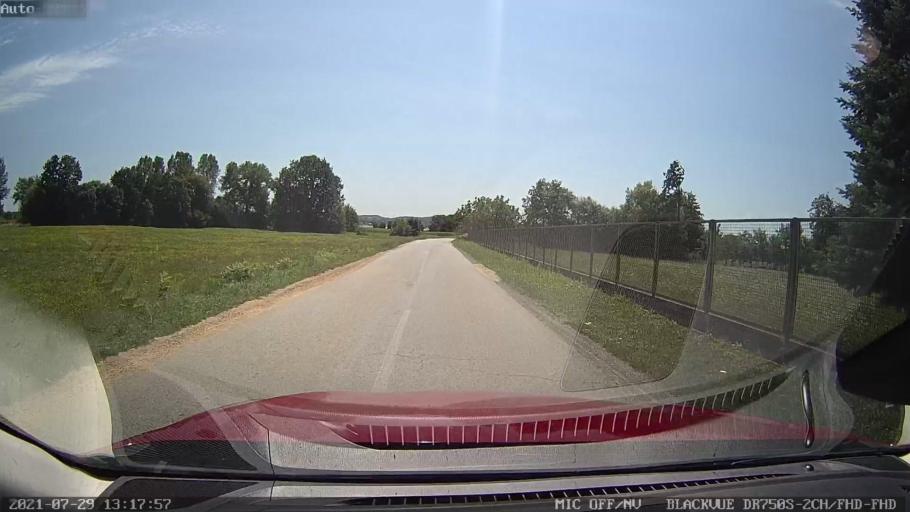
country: HR
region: Varazdinska
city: Varazdin
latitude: 46.2741
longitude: 16.3824
